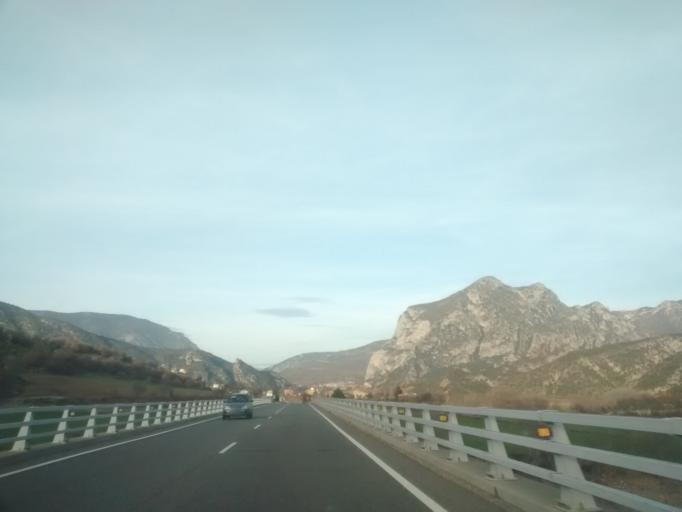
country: ES
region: Catalonia
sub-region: Provincia de Lleida
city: Coll de Nargo
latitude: 42.1615
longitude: 1.3143
